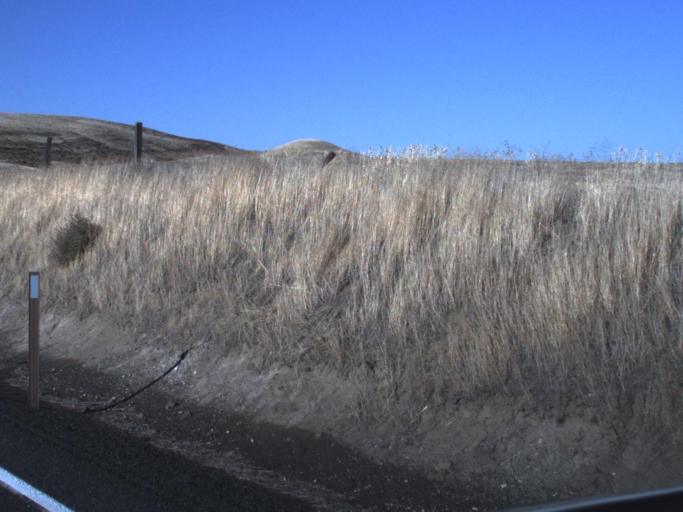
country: US
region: Washington
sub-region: Adams County
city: Ritzville
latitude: 46.8052
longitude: -118.3033
